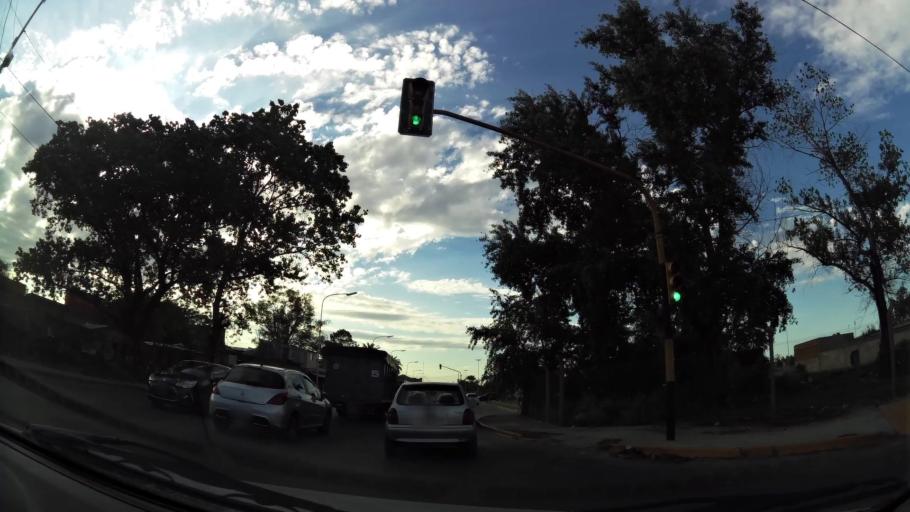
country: AR
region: Buenos Aires
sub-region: Partido de Avellaneda
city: Avellaneda
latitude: -34.6845
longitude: -58.3611
